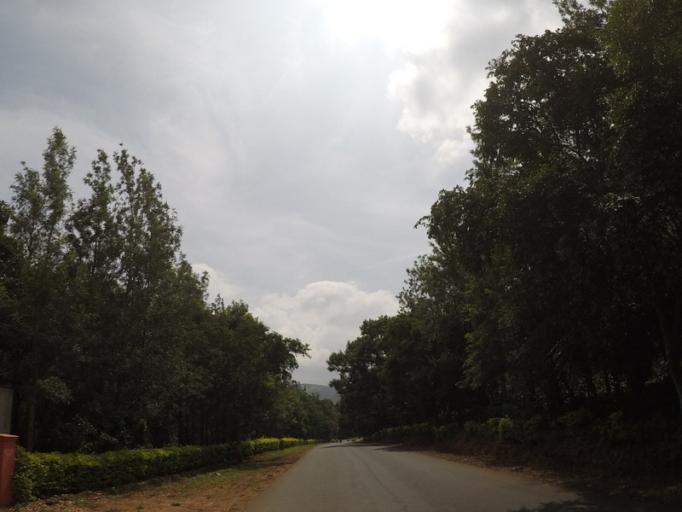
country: IN
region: Karnataka
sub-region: Chikmagalur
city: Chikmagalur
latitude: 13.4107
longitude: 75.7968
